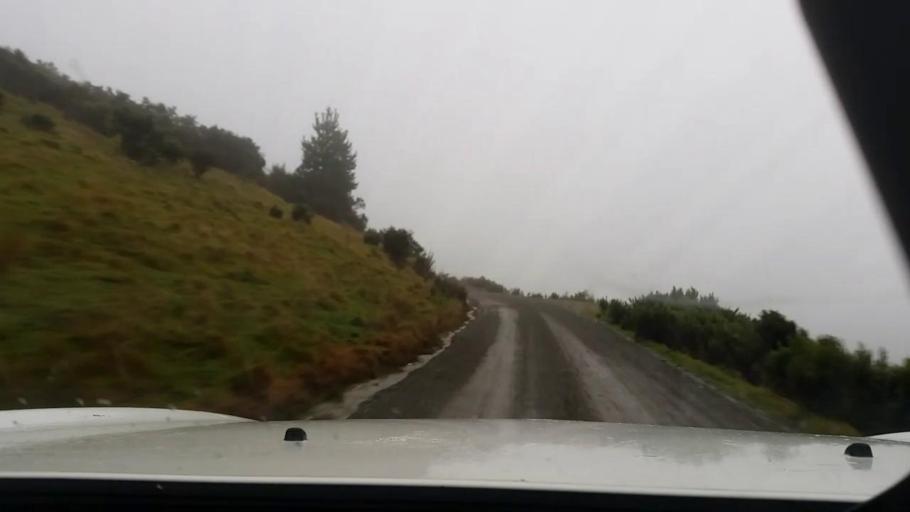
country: NZ
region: Wellington
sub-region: Masterton District
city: Masterton
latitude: -41.2458
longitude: 175.8780
